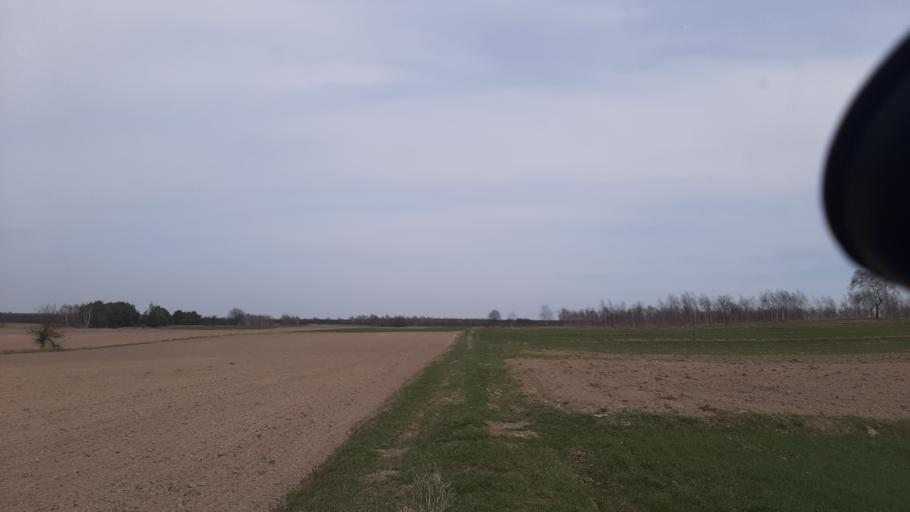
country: PL
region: Lublin Voivodeship
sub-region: Powiat lubelski
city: Jastkow
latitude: 51.3756
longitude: 22.4210
